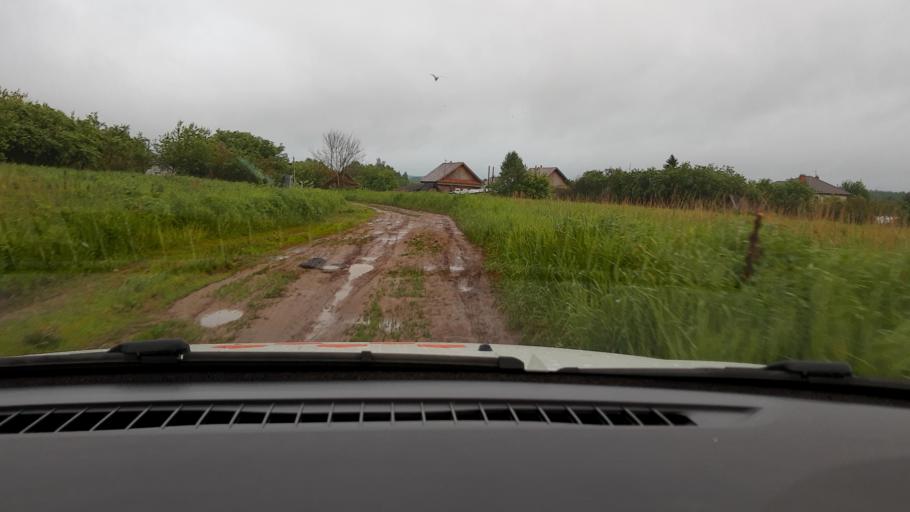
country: RU
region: Nizjnij Novgorod
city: Novaya Balakhna
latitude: 56.6334
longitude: 43.6230
